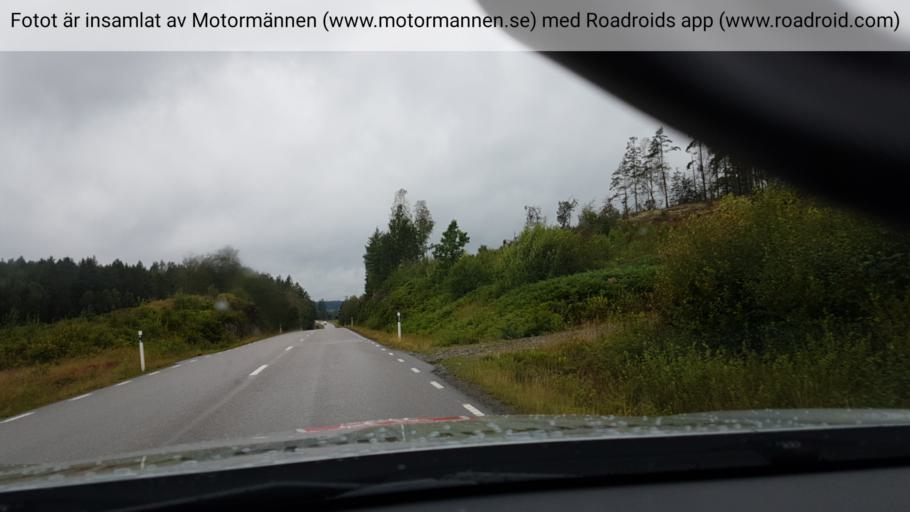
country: SE
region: Vaestra Goetaland
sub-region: Bengtsfors Kommun
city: Billingsfors
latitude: 58.9530
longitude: 12.2234
